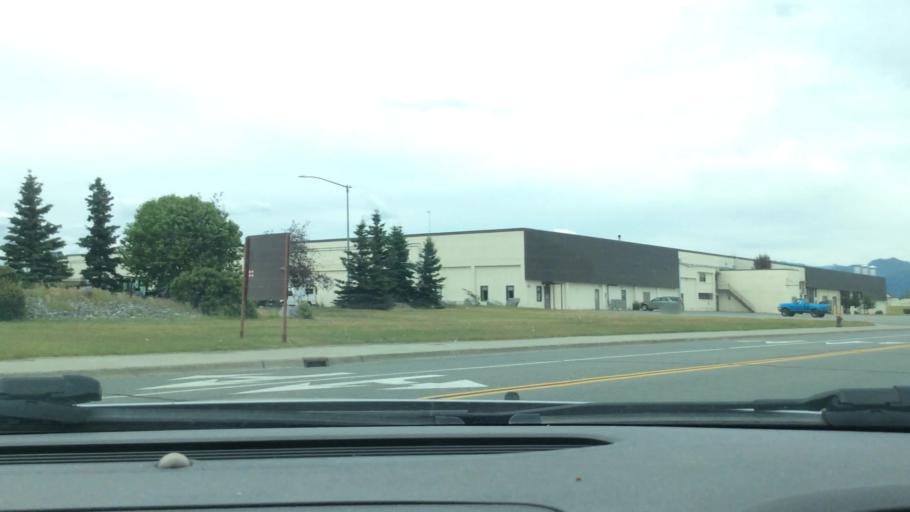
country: US
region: Alaska
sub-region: Anchorage Municipality
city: Anchorage
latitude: 61.2388
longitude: -149.8498
